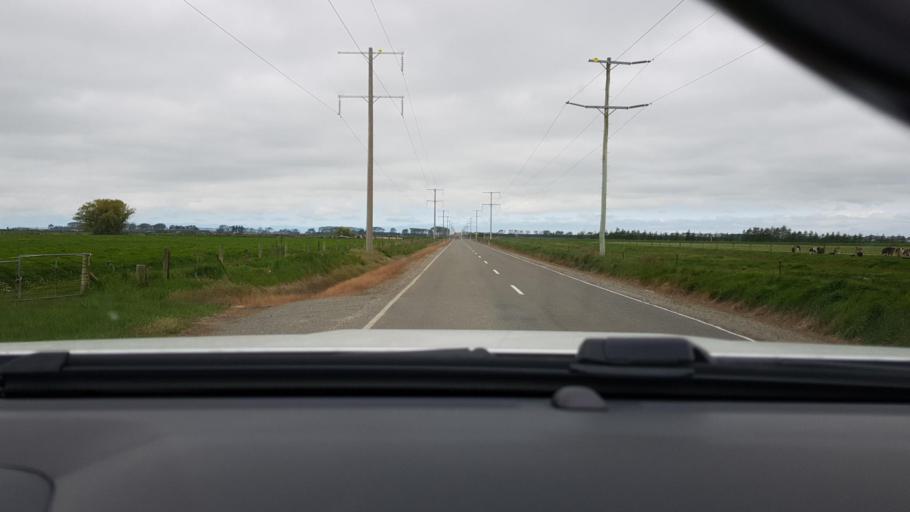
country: NZ
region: Otago
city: Oamaru
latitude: -44.9648
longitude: 170.9940
